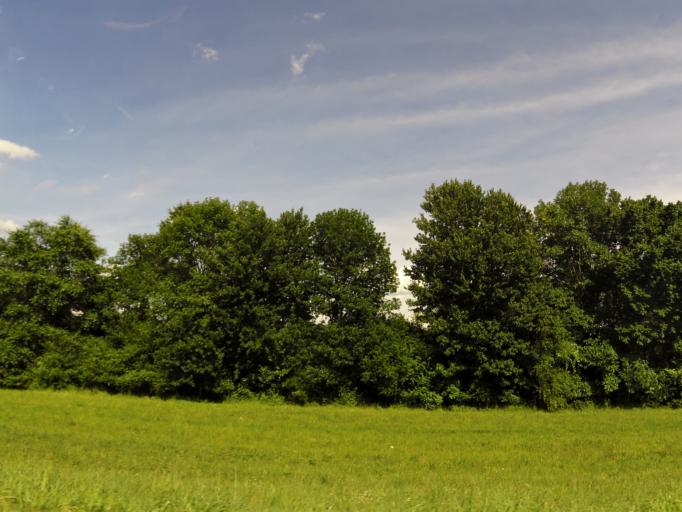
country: US
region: Tennessee
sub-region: Carroll County
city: Huntingdon
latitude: 36.0084
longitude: -88.4458
